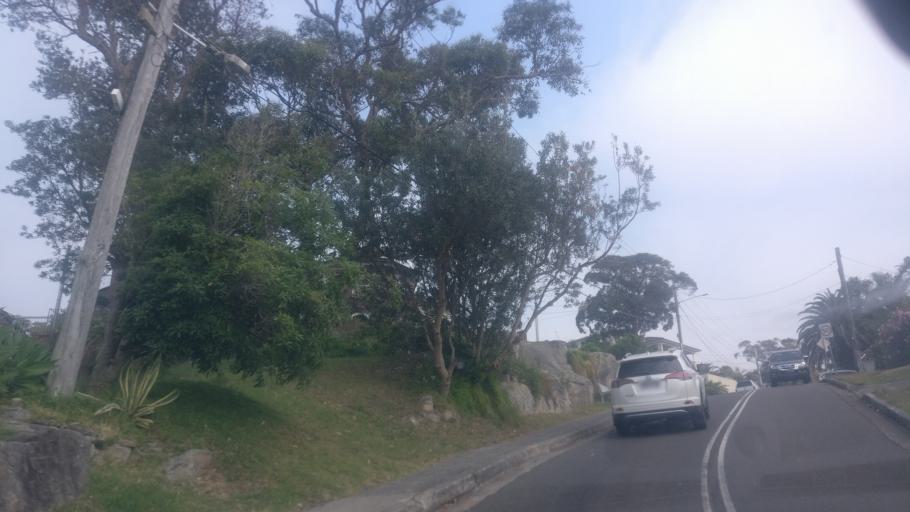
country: AU
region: New South Wales
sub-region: Warringah
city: Dee Why
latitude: -33.7322
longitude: 151.2963
